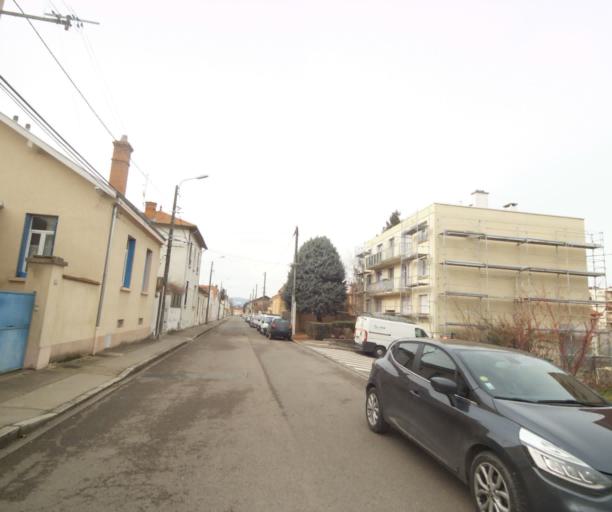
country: FR
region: Rhone-Alpes
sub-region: Departement de la Loire
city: Roanne
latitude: 46.0281
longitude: 4.0580
